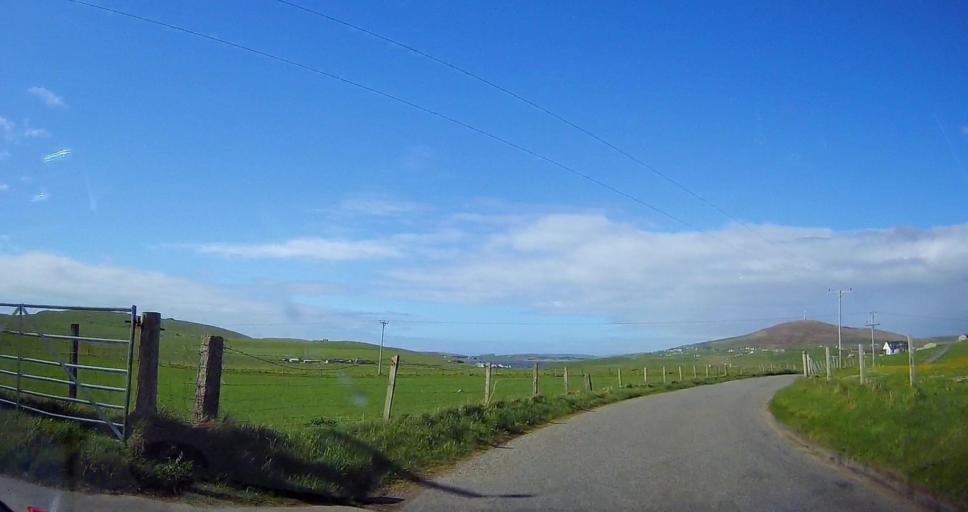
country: GB
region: Scotland
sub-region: Shetland Islands
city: Sandwick
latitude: 59.9131
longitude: -1.3240
